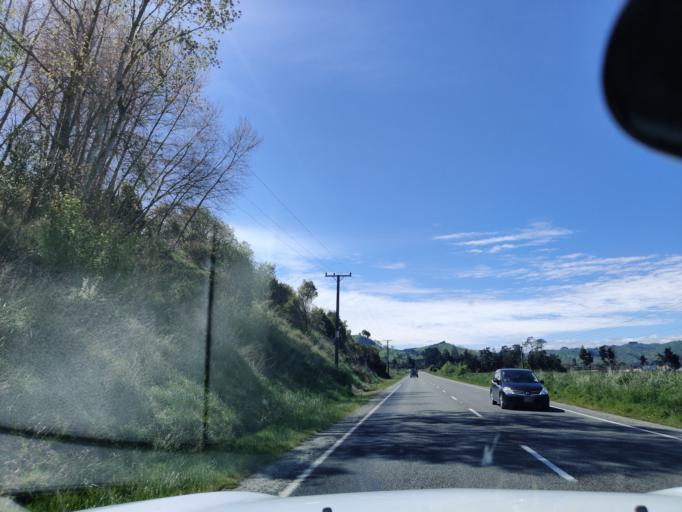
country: NZ
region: Manawatu-Wanganui
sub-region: Ruapehu District
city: Waiouru
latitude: -39.8501
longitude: 175.7336
